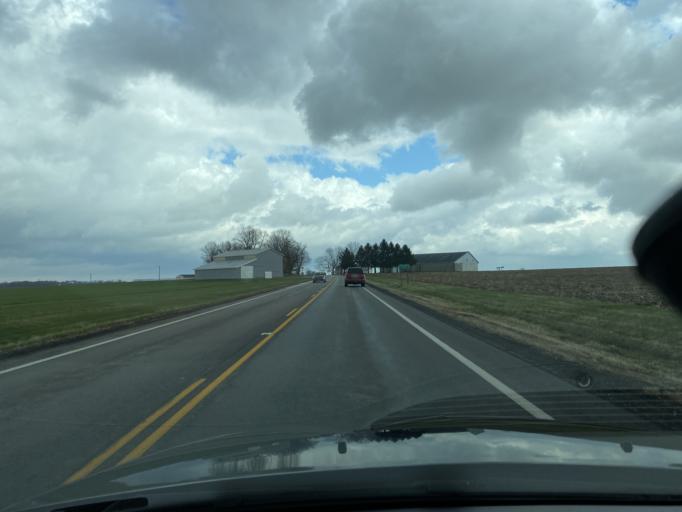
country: US
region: Ohio
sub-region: Wayne County
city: Smithville
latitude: 40.8481
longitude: -81.8800
